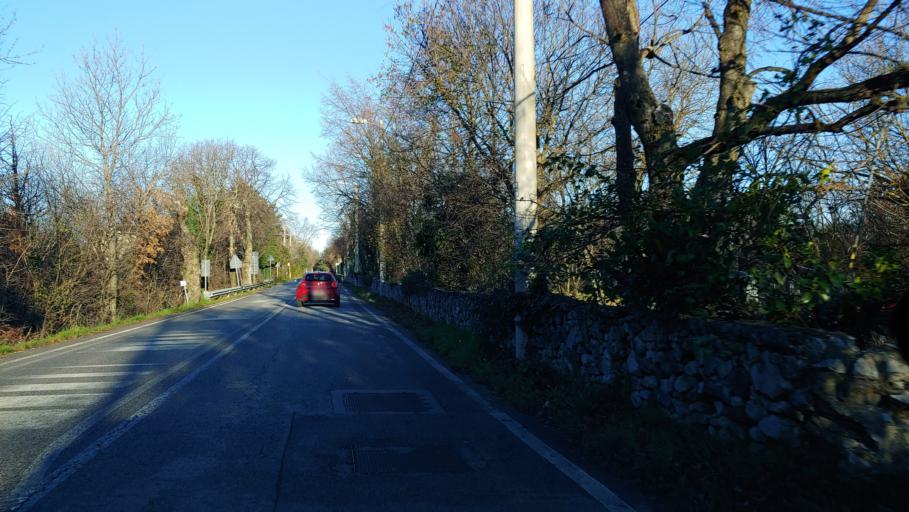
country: IT
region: Friuli Venezia Giulia
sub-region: Provincia di Trieste
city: Trieste
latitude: 45.6621
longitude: 13.8351
